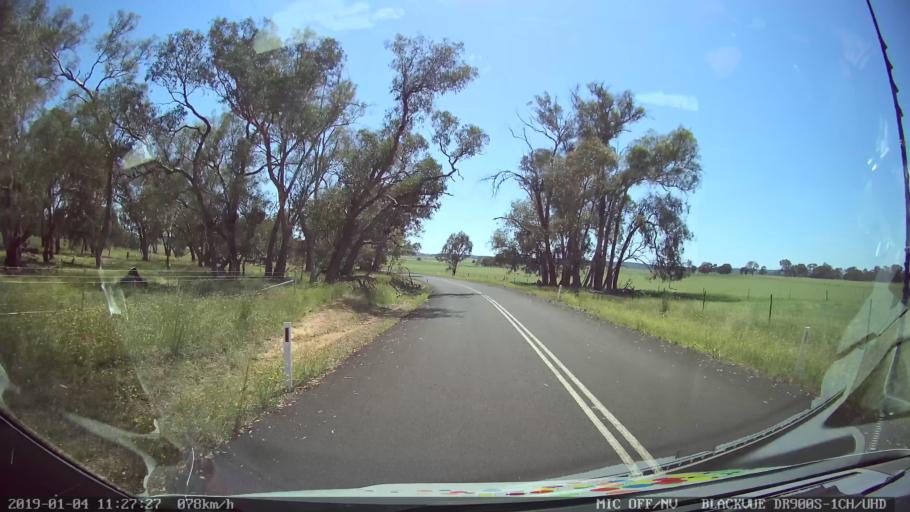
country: AU
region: New South Wales
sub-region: Cabonne
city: Molong
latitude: -33.1089
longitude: 148.7631
